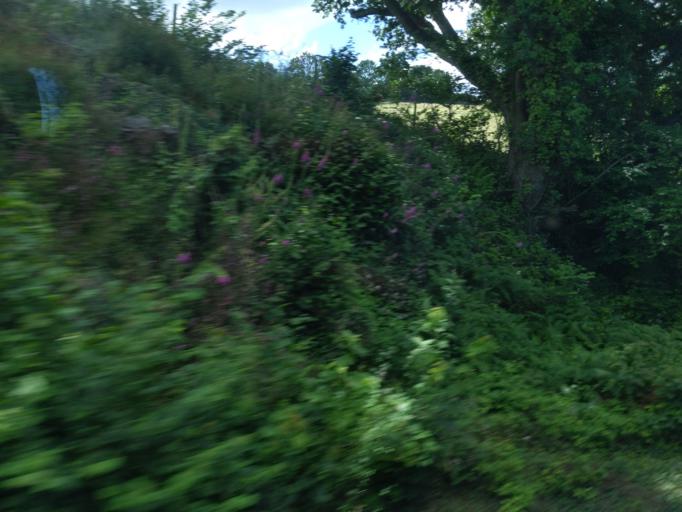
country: GB
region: England
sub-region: Cornwall
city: Par
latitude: 50.3612
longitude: -4.6991
